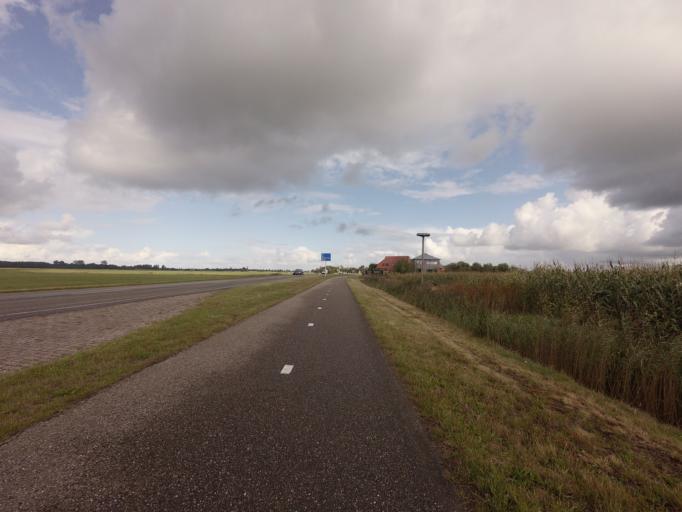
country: NL
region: Friesland
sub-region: Gemeente Tytsjerksteradiel
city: Garyp
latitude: 53.1554
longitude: 5.9514
